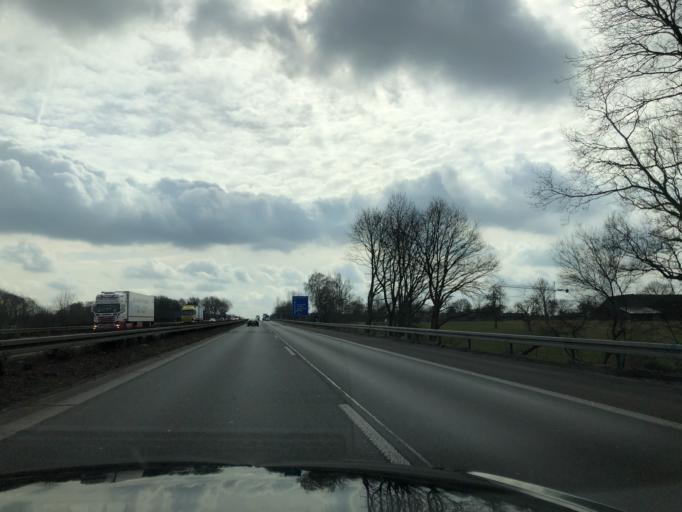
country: DE
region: North Rhine-Westphalia
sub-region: Regierungsbezirk Dusseldorf
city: Dinslaken
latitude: 51.5691
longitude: 6.8026
